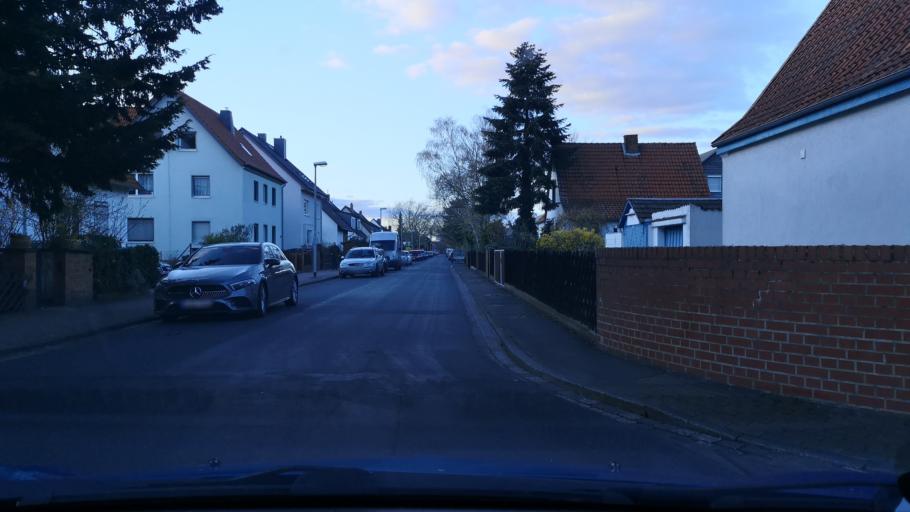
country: DE
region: Lower Saxony
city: Langenhagen
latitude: 52.4112
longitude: 9.7872
